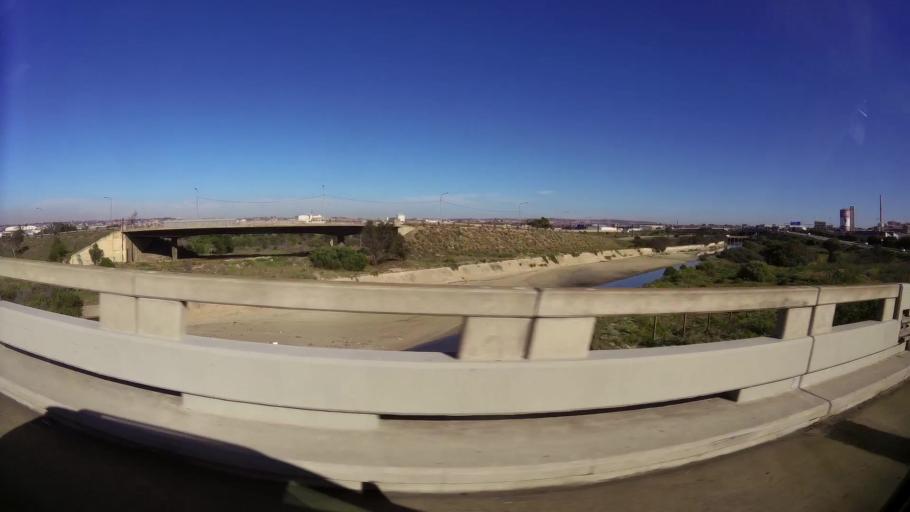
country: ZA
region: Eastern Cape
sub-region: Nelson Mandela Bay Metropolitan Municipality
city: Port Elizabeth
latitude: -33.9163
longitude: 25.6099
